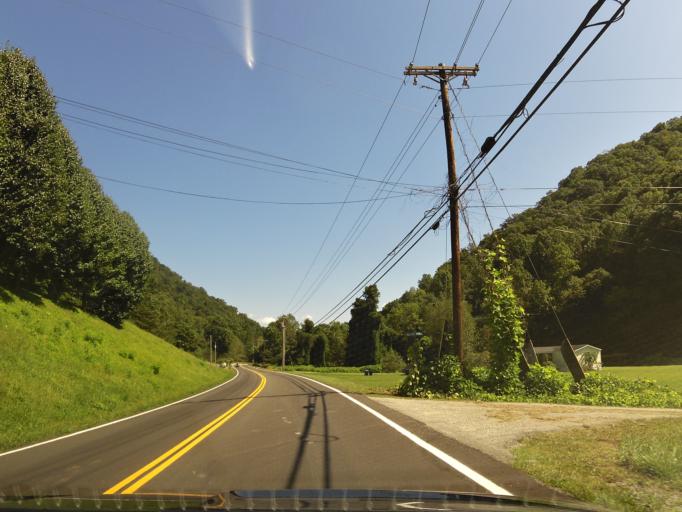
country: US
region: Kentucky
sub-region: Clay County
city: Manchester
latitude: 37.1290
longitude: -83.6236
